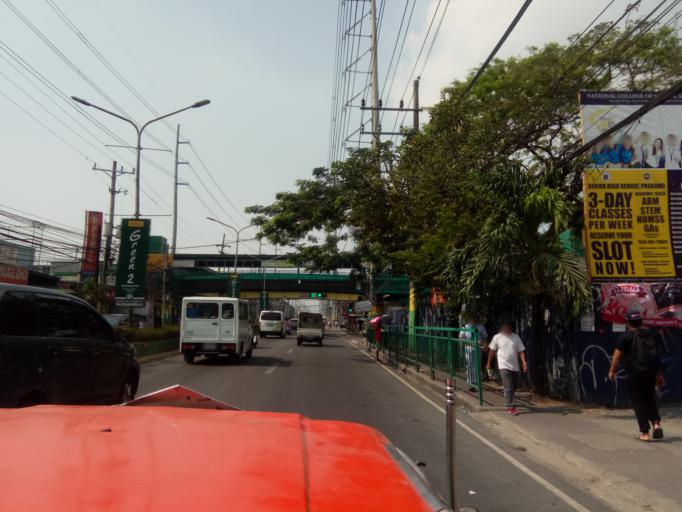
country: PH
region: Calabarzon
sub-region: Province of Cavite
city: Dasmarinas
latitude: 14.3258
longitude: 120.9406
